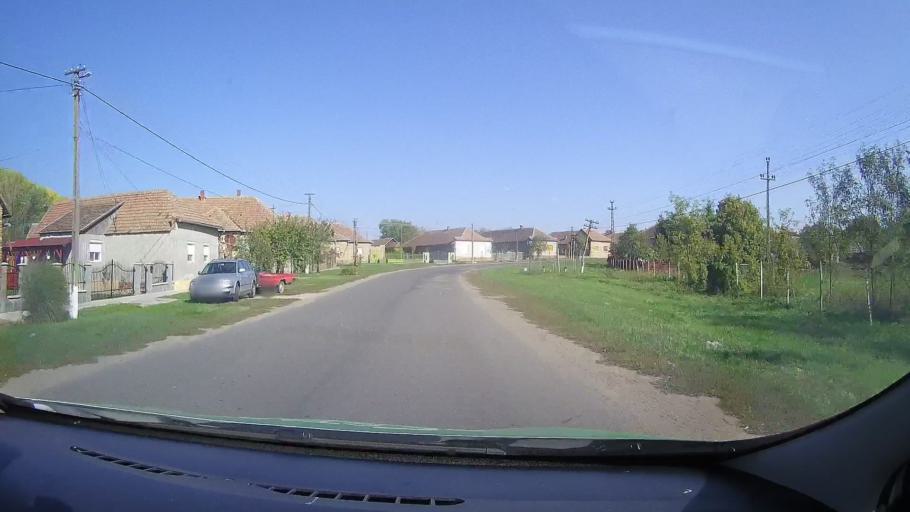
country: RO
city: Foieni
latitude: 47.6965
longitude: 22.3763
